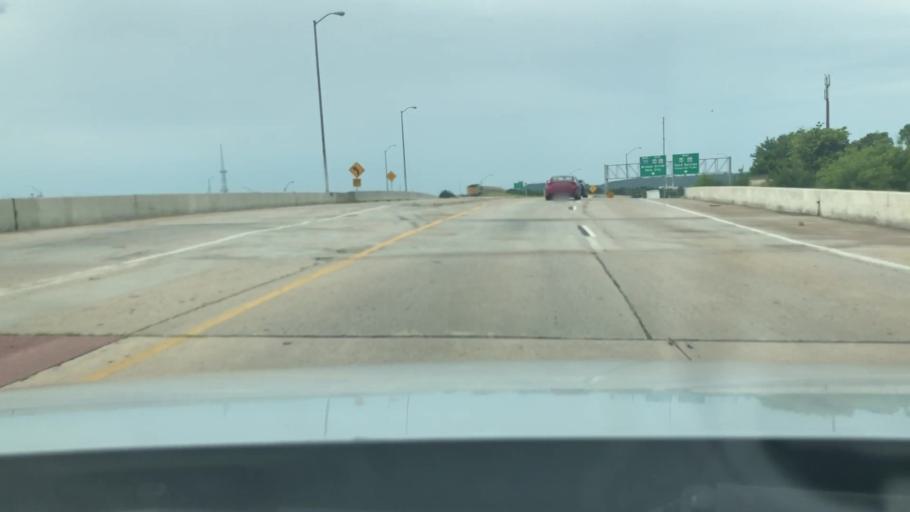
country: US
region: Oklahoma
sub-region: Tulsa County
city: Tulsa
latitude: 36.1616
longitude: -96.0009
